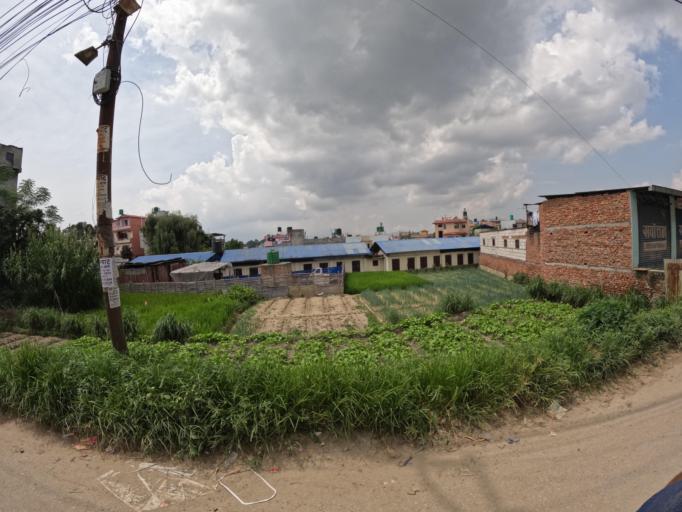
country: NP
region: Central Region
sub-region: Bagmati Zone
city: Bhaktapur
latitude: 27.6878
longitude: 85.3826
